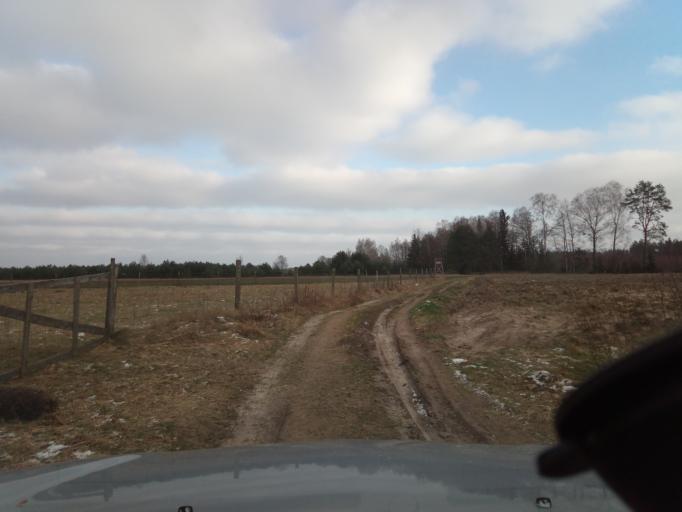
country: LT
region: Alytaus apskritis
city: Druskininkai
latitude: 54.1106
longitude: 24.2241
